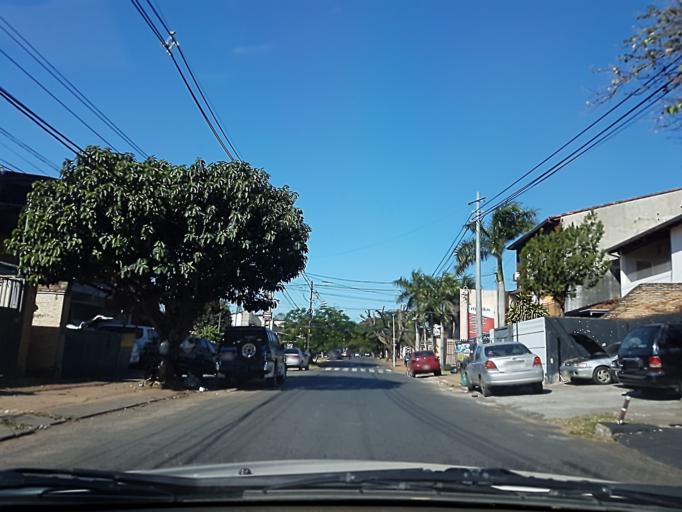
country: PY
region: Central
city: Fernando de la Mora
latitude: -25.2997
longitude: -57.5654
